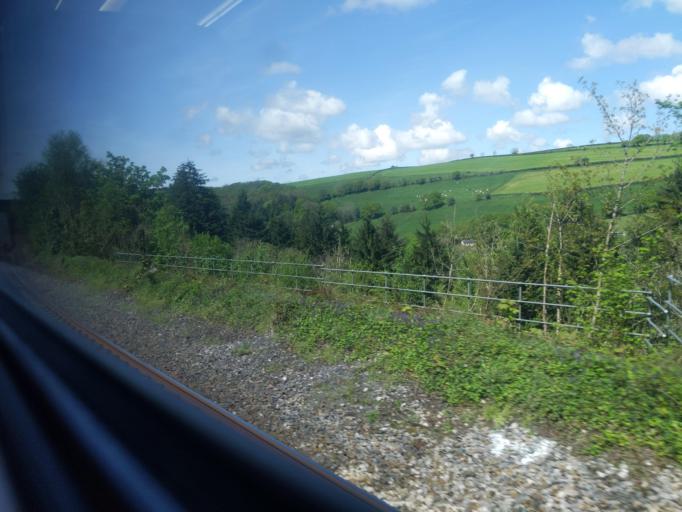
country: GB
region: England
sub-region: Cornwall
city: Lostwithiel
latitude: 50.4550
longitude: -4.5913
